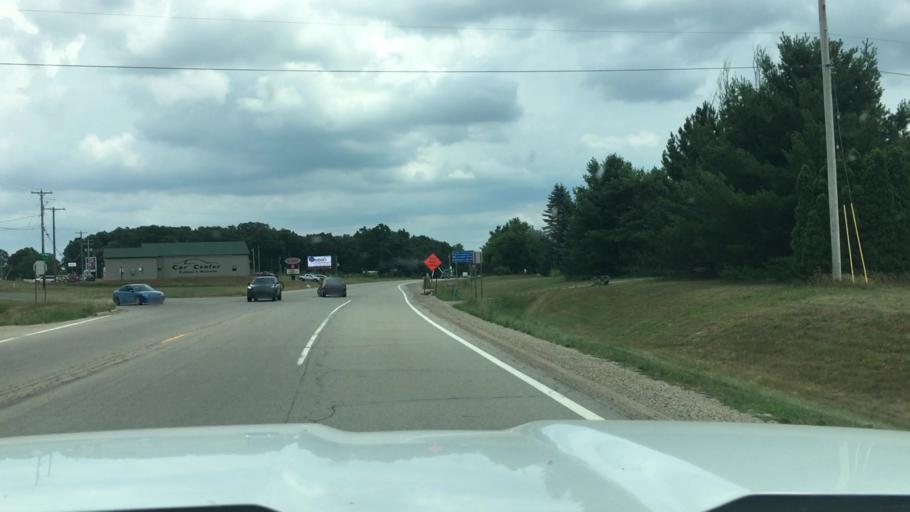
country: US
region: Michigan
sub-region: Montcalm County
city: Greenville
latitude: 43.1761
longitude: -85.3578
